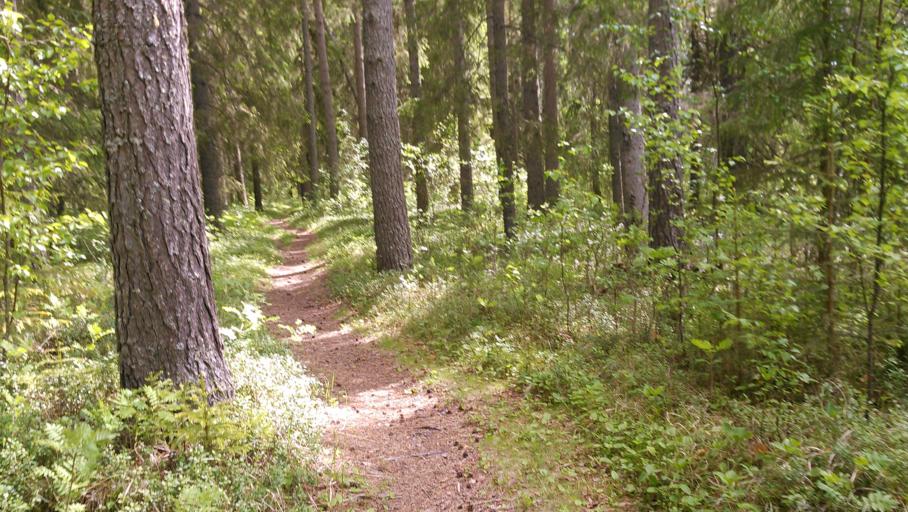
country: SE
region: Vaesterbotten
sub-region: Vannas Kommun
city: Vannasby
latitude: 64.0143
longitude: 19.9035
